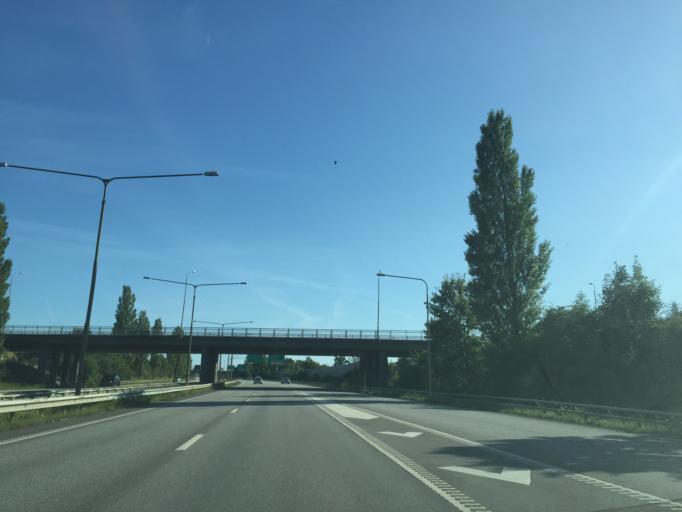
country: SE
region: Skane
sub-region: Malmo
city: Tygelsjo
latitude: 55.5612
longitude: 13.0001
